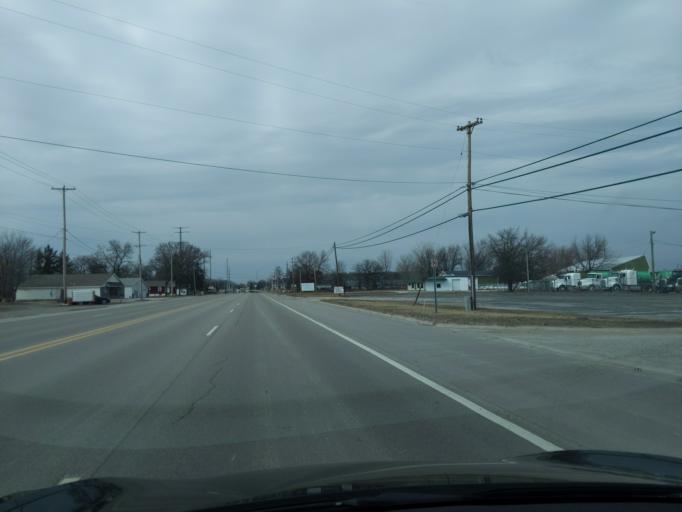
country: US
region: Michigan
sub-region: Bay County
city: Bay City
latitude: 43.6622
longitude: -83.9491
